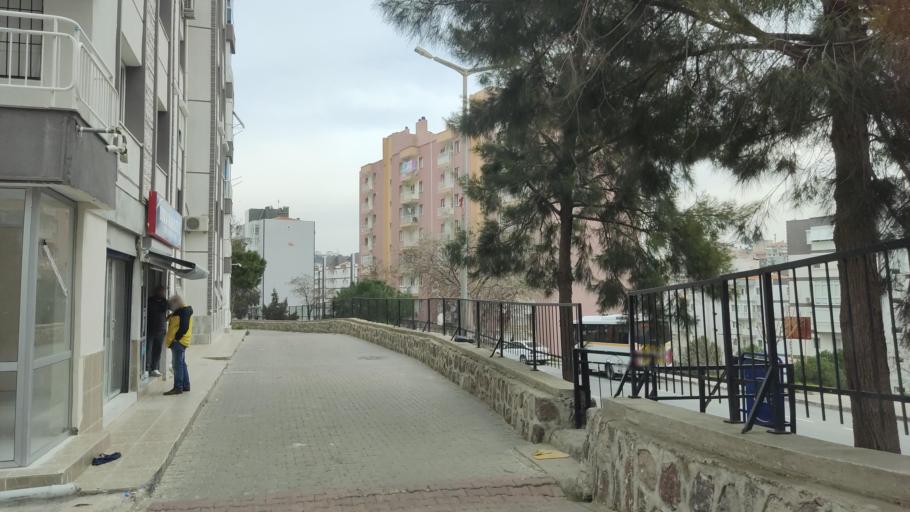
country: TR
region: Izmir
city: Karsiyaka
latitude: 38.5039
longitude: 27.0716
